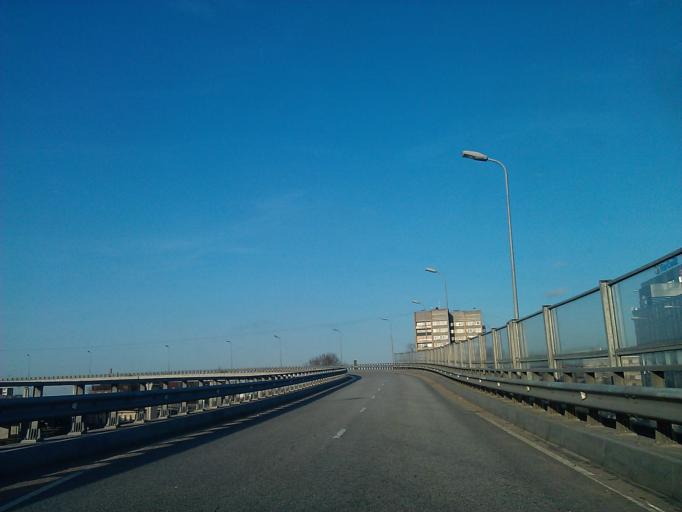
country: LV
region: Riga
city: Riga
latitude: 56.9214
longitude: 24.1669
